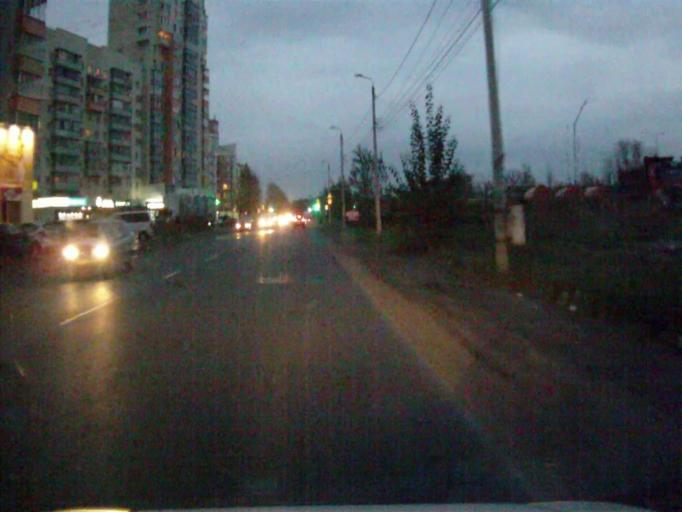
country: RU
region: Chelyabinsk
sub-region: Gorod Chelyabinsk
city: Chelyabinsk
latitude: 55.1613
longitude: 61.2961
